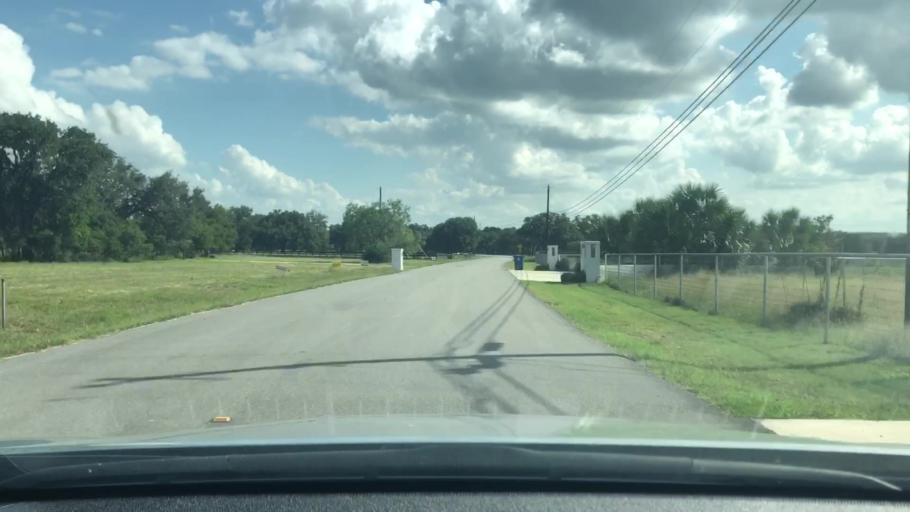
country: US
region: Texas
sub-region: Bexar County
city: Fair Oaks Ranch
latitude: 29.7658
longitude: -98.6308
